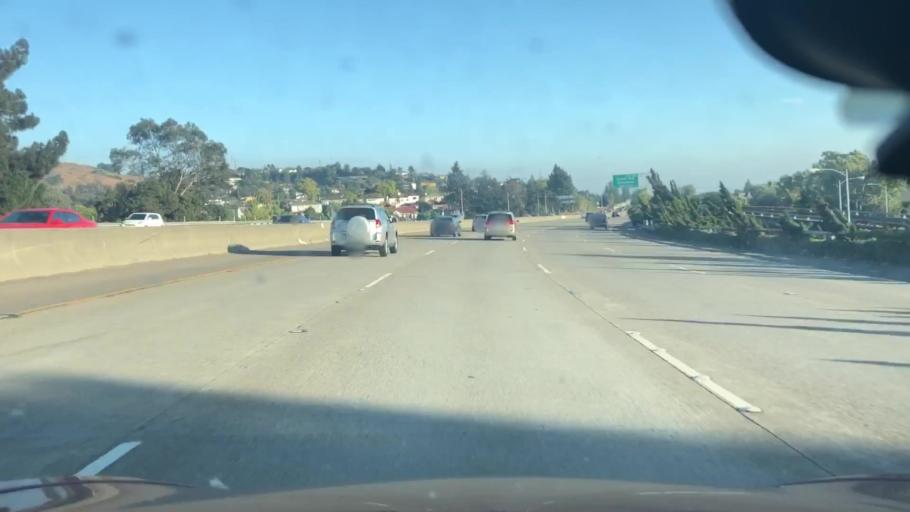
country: US
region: California
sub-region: Alameda County
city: San Leandro
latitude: 37.7370
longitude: -122.1403
